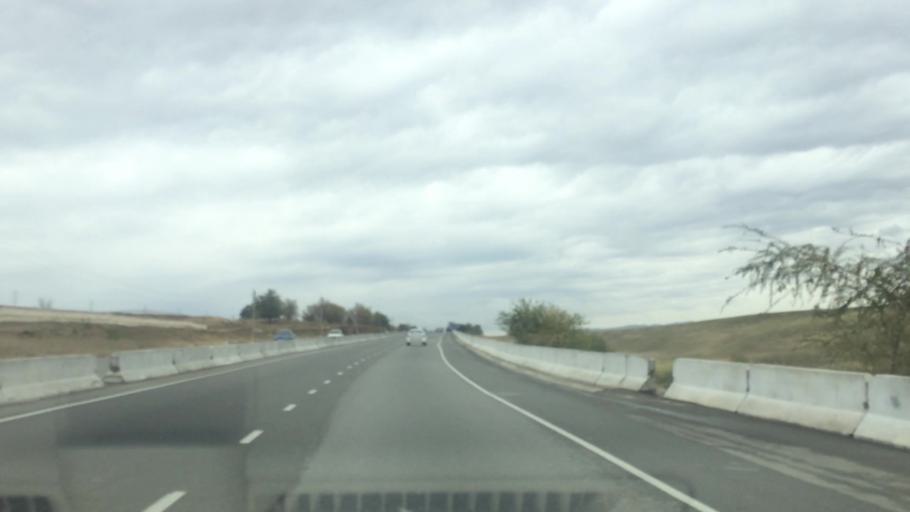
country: UZ
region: Samarqand
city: Bulung'ur
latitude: 39.9484
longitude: 67.5358
